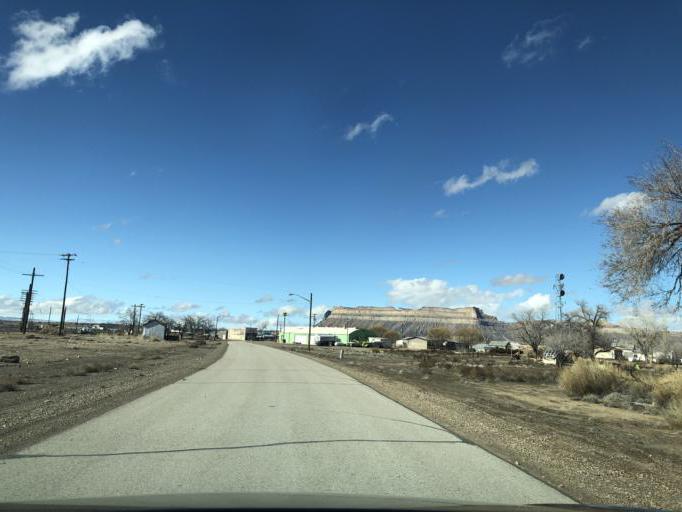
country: US
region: Utah
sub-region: Carbon County
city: East Carbon City
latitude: 38.9917
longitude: -110.1630
